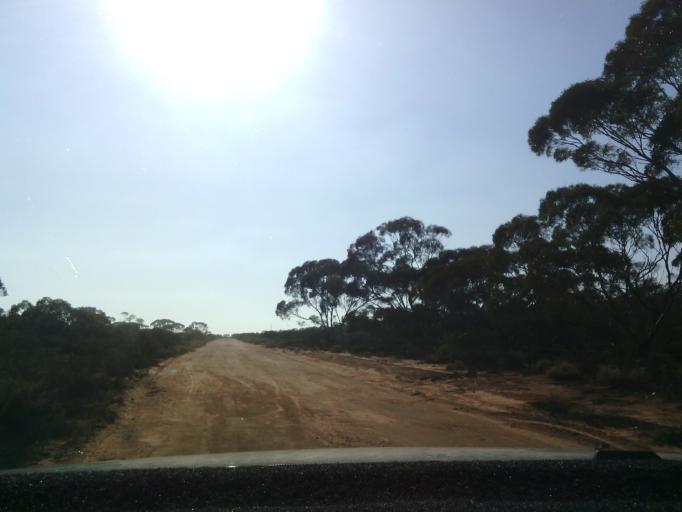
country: AU
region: South Australia
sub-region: Berri and Barmera
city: Monash
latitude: -34.2250
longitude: 140.5809
